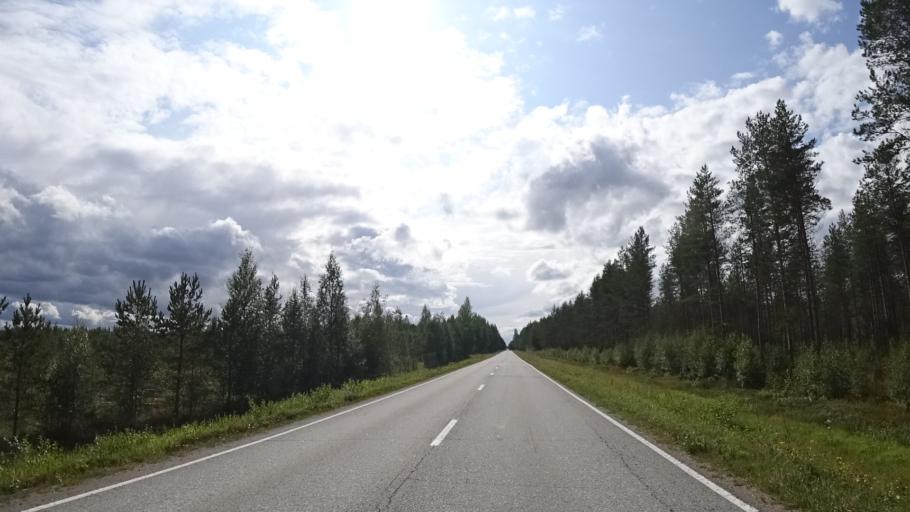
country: FI
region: North Karelia
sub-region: Joensuu
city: Ilomantsi
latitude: 62.7640
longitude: 31.0262
